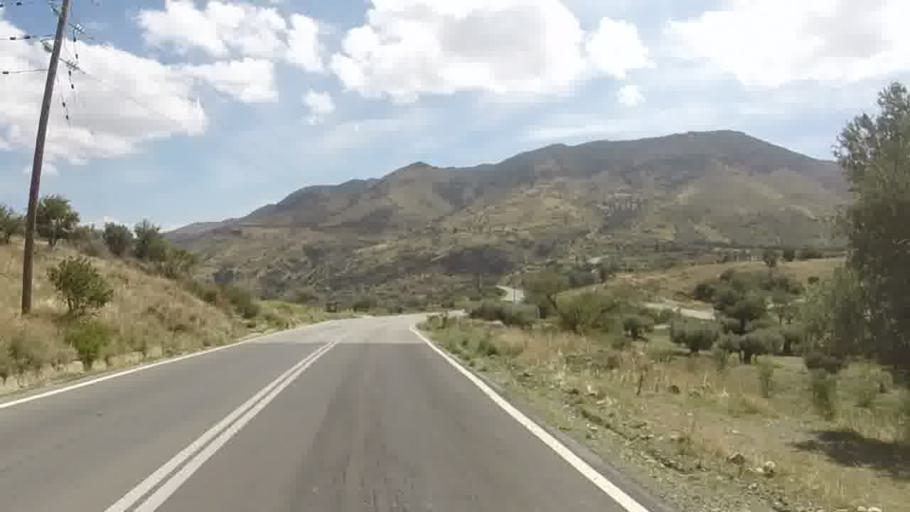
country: GR
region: Crete
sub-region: Nomos Rethymnis
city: Agia Galini
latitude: 35.1476
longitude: 24.6331
